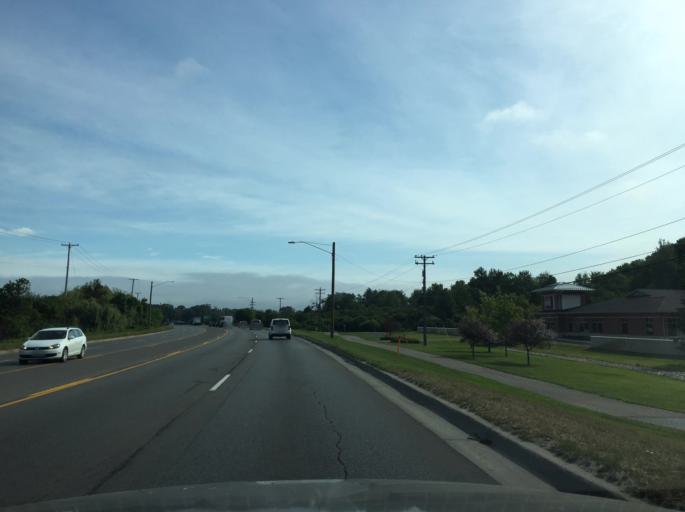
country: US
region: Michigan
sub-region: Grand Traverse County
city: Traverse City
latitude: 44.7472
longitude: -85.6369
